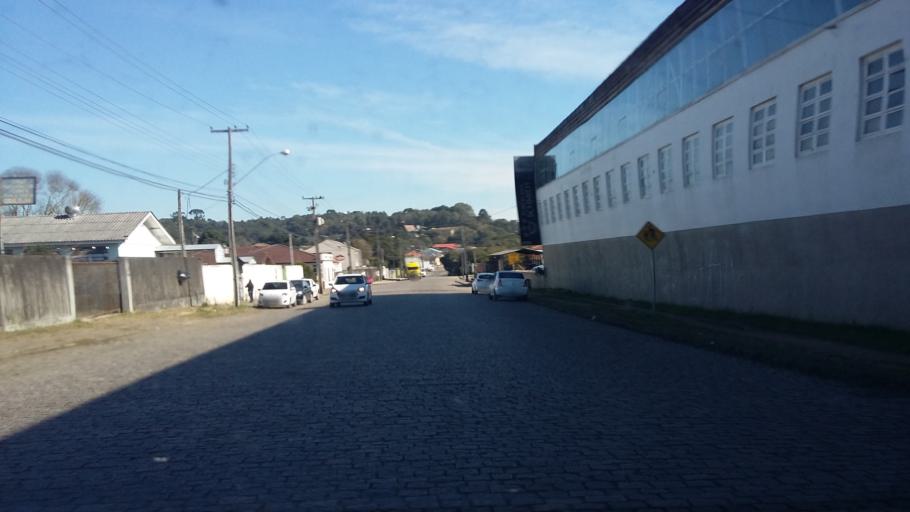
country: BR
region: Parana
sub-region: Campo Largo
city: Campo Largo
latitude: -25.4669
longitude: -49.5720
